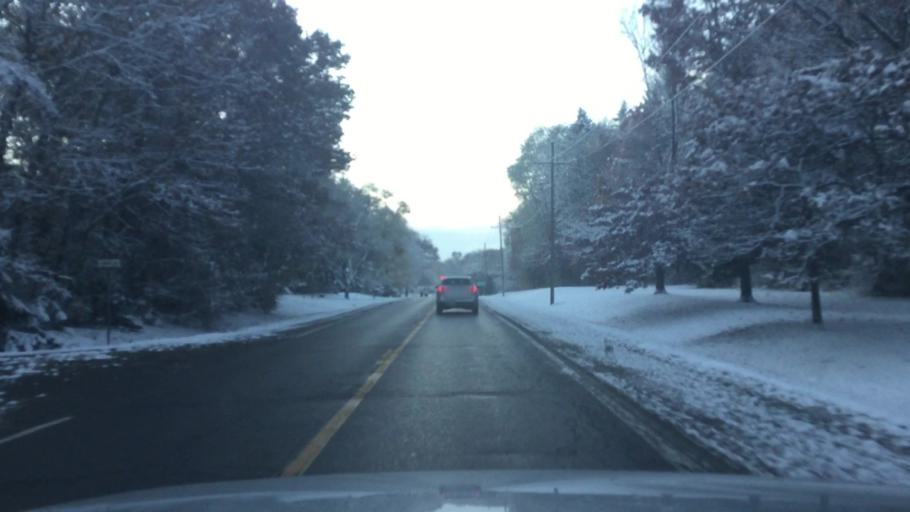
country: US
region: Michigan
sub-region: Oakland County
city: Wolverine Lake
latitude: 42.5731
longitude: -83.4700
